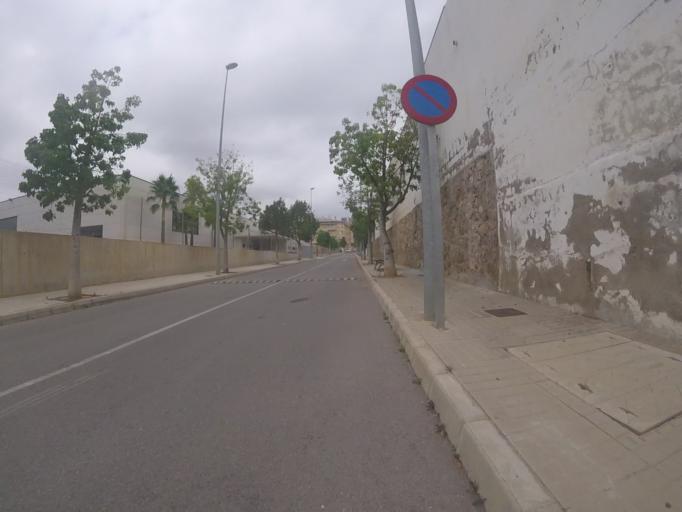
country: ES
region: Valencia
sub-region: Provincia de Castello
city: Cabanes
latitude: 40.1526
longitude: 0.0473
